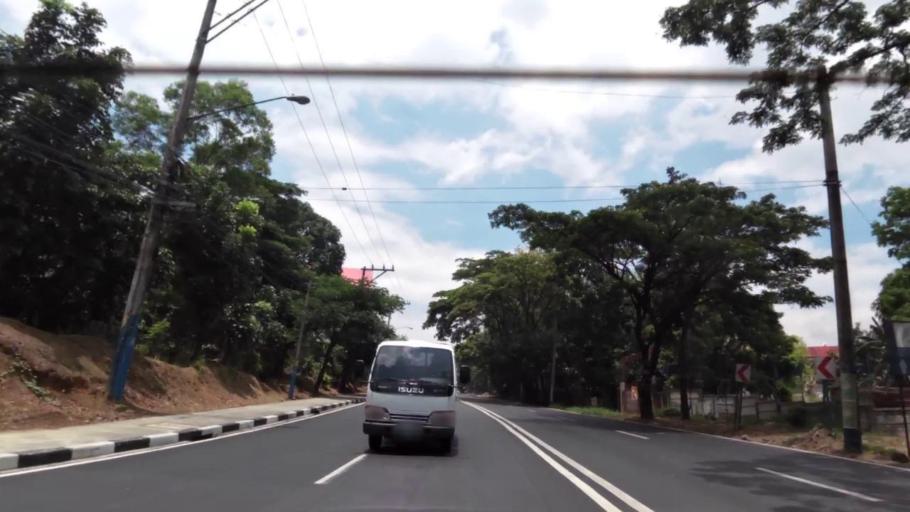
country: PH
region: Calabarzon
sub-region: Province of Rizal
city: Antipolo
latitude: 14.6105
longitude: 121.1595
